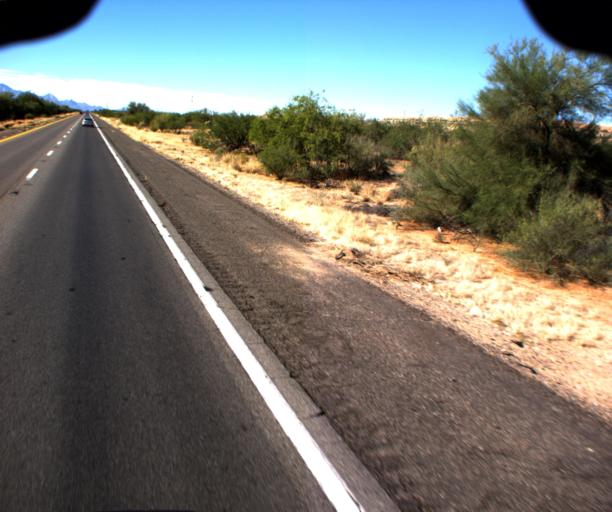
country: US
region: Arizona
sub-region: Pima County
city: Sahuarita
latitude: 31.9835
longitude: -110.9914
